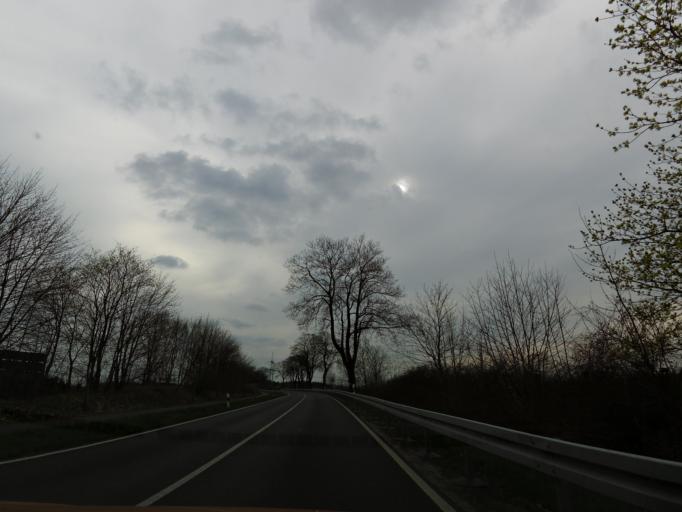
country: DE
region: Brandenburg
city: Mullrose
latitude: 52.2801
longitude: 14.4463
